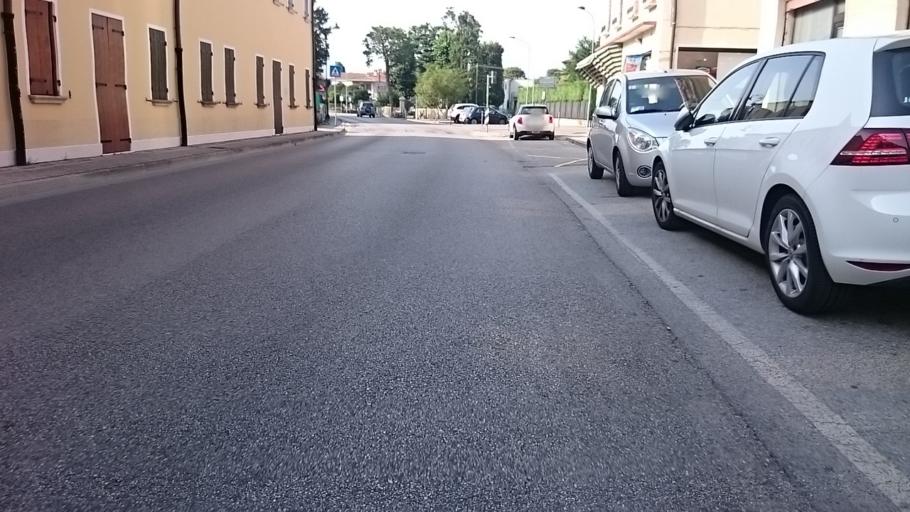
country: IT
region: Veneto
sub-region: Provincia di Venezia
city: Vigonovo
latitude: 45.3871
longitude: 12.0078
